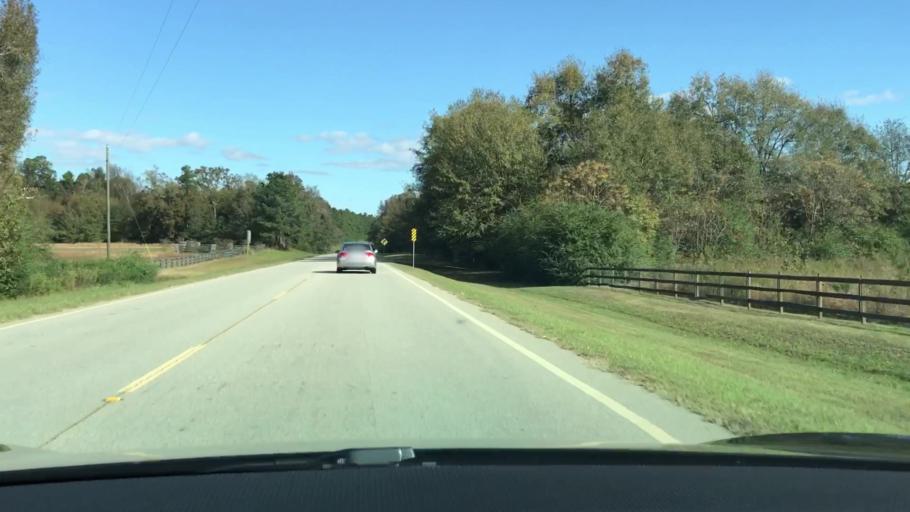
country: US
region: Georgia
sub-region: Jefferson County
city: Wrens
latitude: 33.2344
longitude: -82.4578
